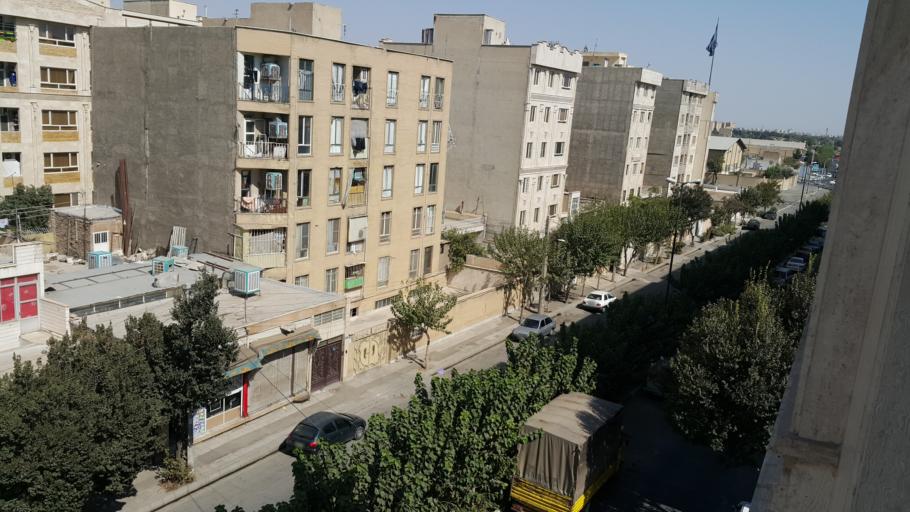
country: IR
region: Tehran
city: Rey
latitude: 35.5835
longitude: 51.4298
